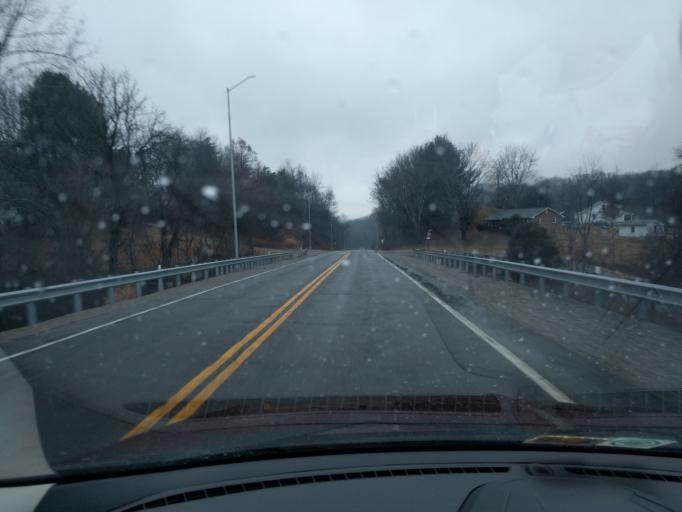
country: US
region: Virginia
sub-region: Pulaski County
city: Pulaski
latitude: 37.0361
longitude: -80.7355
